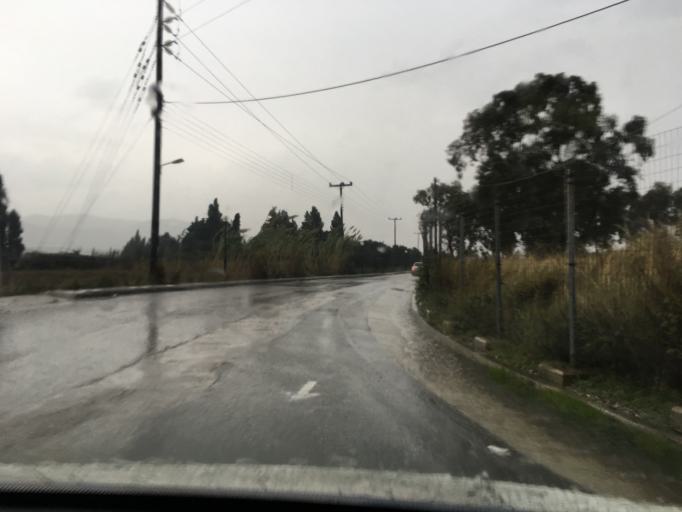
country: GR
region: West Greece
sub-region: Nomos Aitolias kai Akarnanias
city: Antirrio
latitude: 38.3355
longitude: 21.7656
